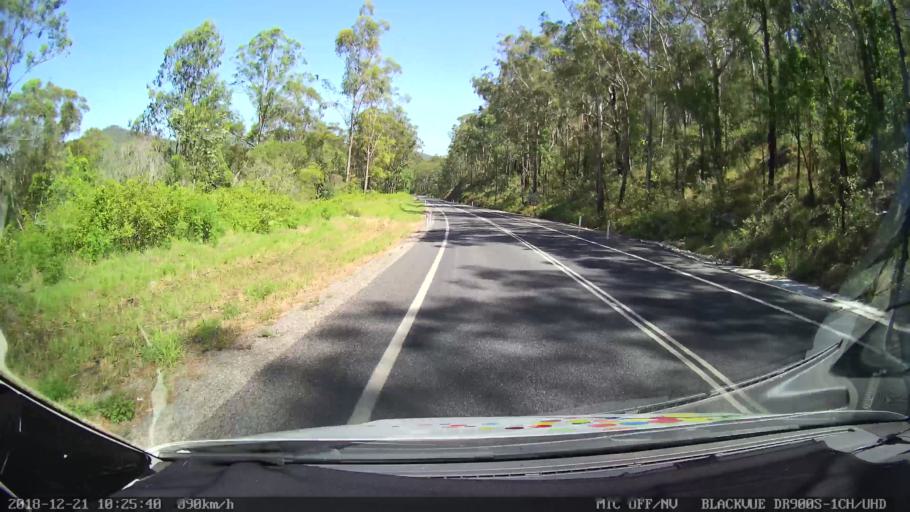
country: AU
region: New South Wales
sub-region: Clarence Valley
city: South Grafton
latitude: -29.6325
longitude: 152.7619
